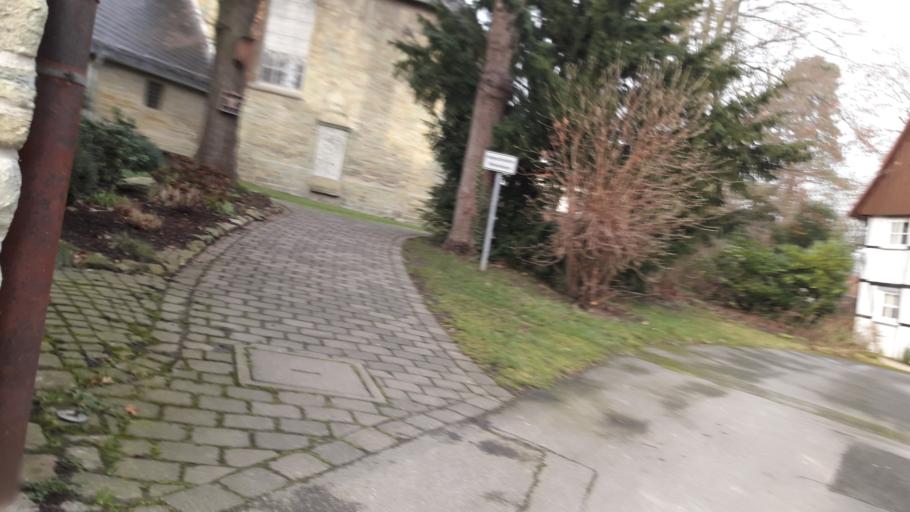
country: DE
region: North Rhine-Westphalia
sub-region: Regierungsbezirk Arnsberg
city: Soest
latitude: 51.5771
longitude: 8.0352
